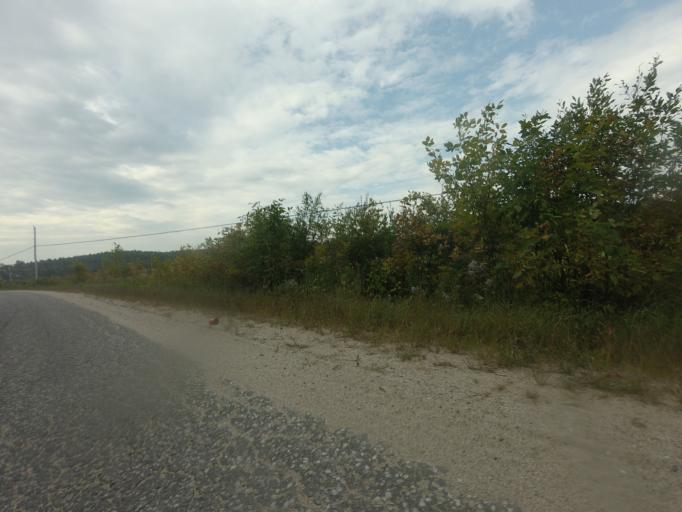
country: CA
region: Quebec
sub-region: Outaouais
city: Wakefield
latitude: 45.9785
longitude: -75.9341
